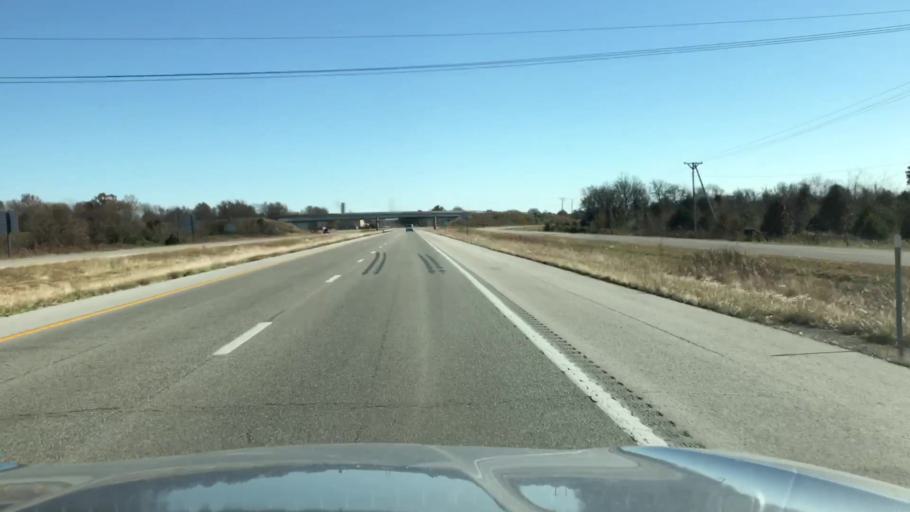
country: US
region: Missouri
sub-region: Jasper County
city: Carthage
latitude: 37.1355
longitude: -94.3170
